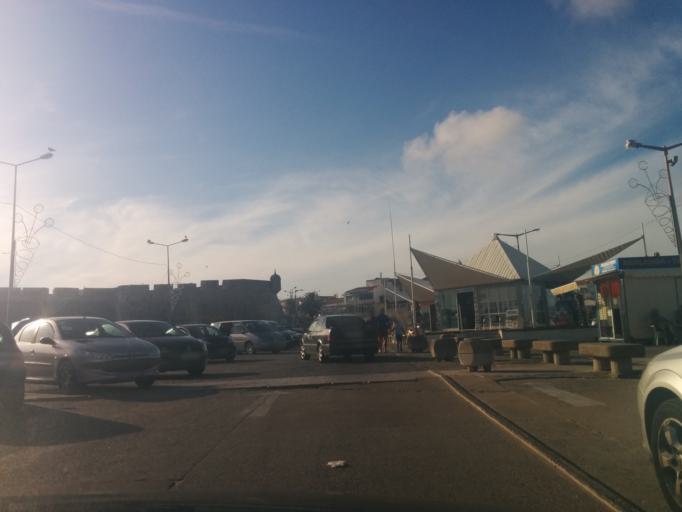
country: PT
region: Leiria
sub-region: Peniche
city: Peniche
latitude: 39.3529
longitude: -9.3785
